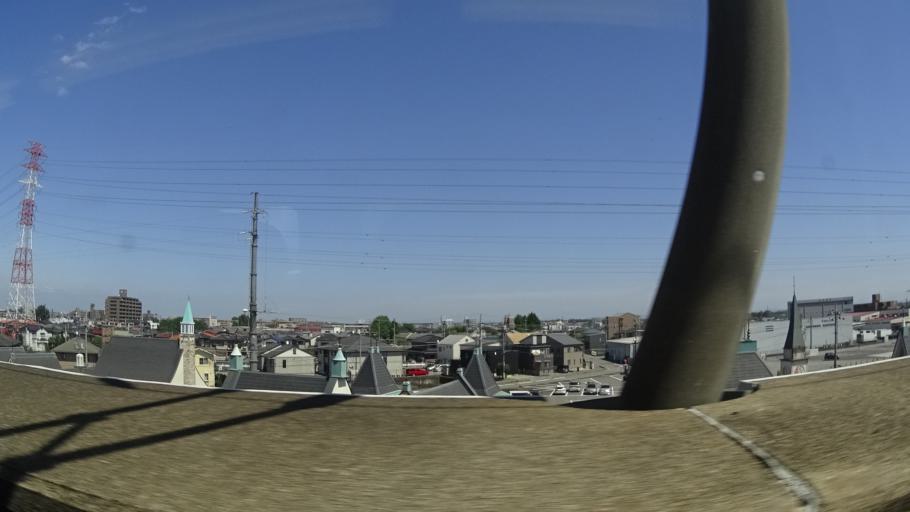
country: JP
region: Tochigi
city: Utsunomiya-shi
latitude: 36.5383
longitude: 139.8934
